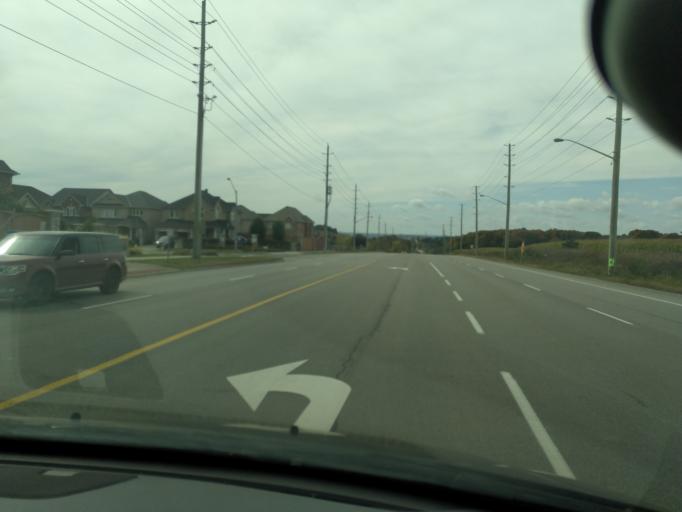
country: CA
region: Ontario
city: Newmarket
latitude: 44.0695
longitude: -79.5002
